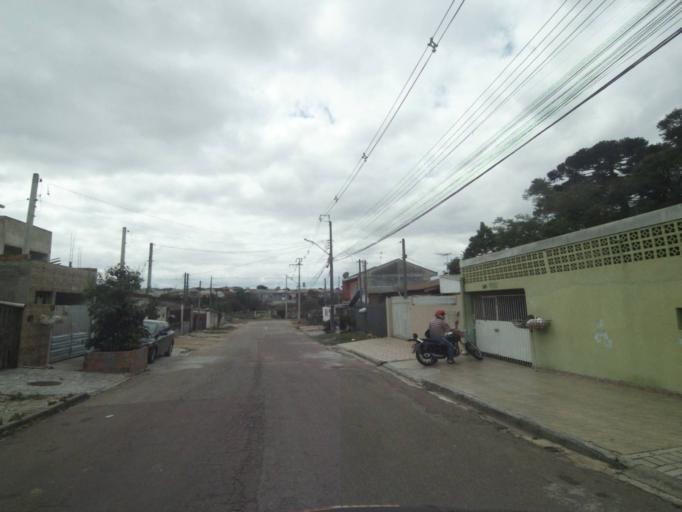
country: BR
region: Parana
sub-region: Sao Jose Dos Pinhais
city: Sao Jose dos Pinhais
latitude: -25.5546
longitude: -49.2601
